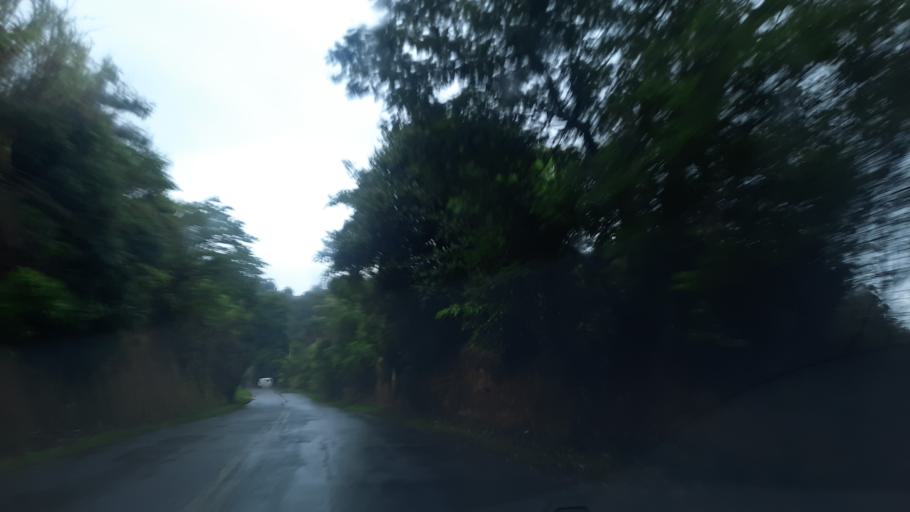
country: BR
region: Sao Paulo
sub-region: Atibaia
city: Atibaia
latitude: -23.0850
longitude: -46.5259
